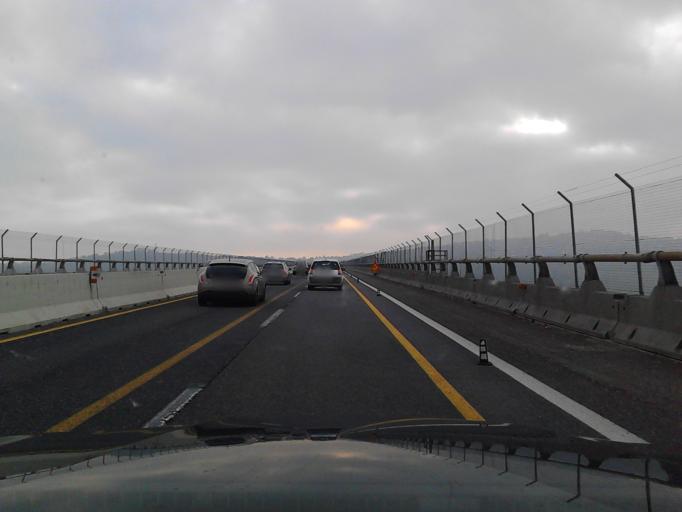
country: IT
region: Abruzzo
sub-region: Provincia di Teramo
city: Tortoreto Lido
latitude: 42.7839
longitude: 13.9350
